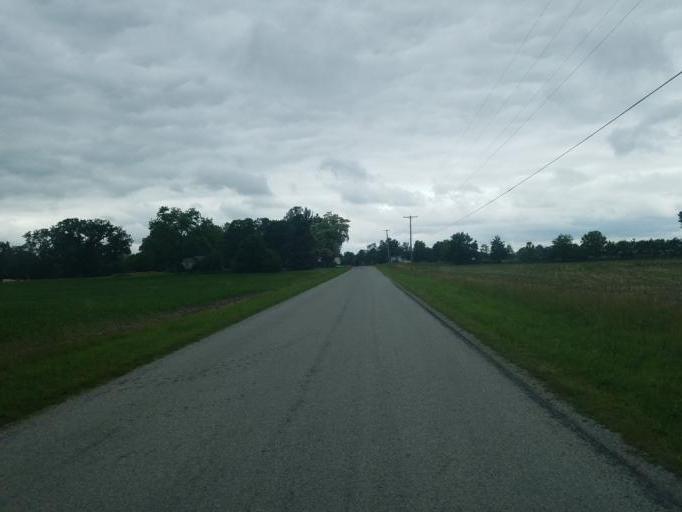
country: US
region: Ohio
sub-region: Marion County
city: Marion
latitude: 40.6939
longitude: -83.1564
